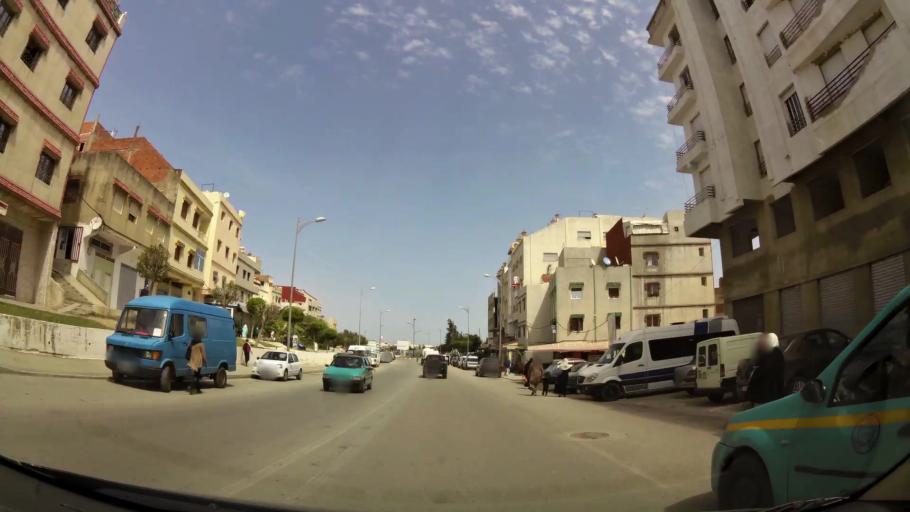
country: MA
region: Tanger-Tetouan
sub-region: Tanger-Assilah
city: Tangier
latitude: 35.7468
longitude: -5.8294
